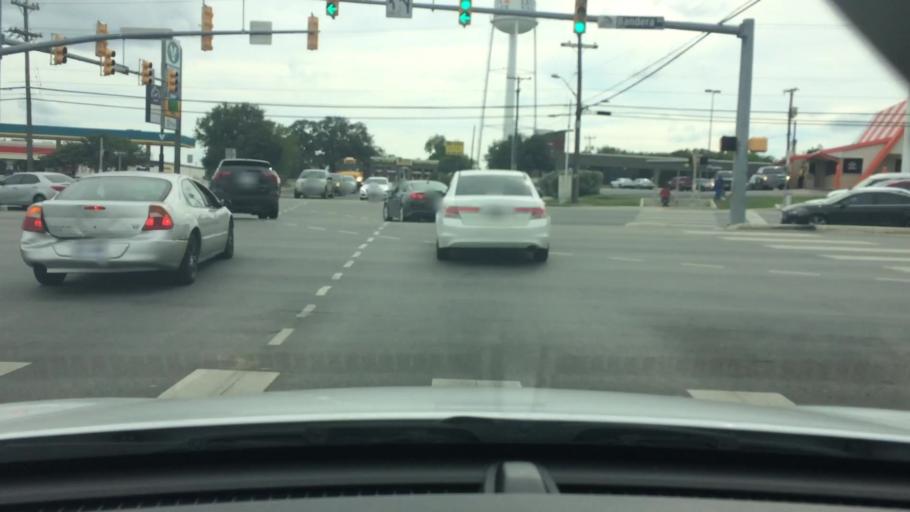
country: US
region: Texas
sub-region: Bexar County
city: Leon Valley
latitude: 29.4996
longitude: -98.6239
